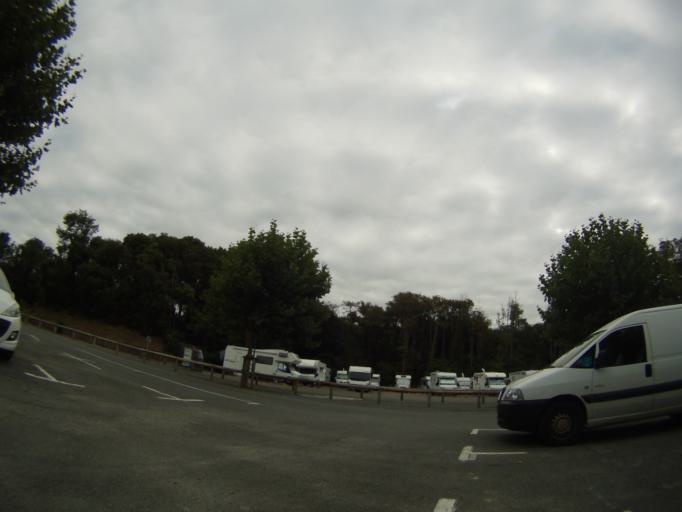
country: FR
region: Pays de la Loire
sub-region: Departement de la Vendee
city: Longeville-sur-Mer
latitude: 46.4030
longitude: -1.5059
